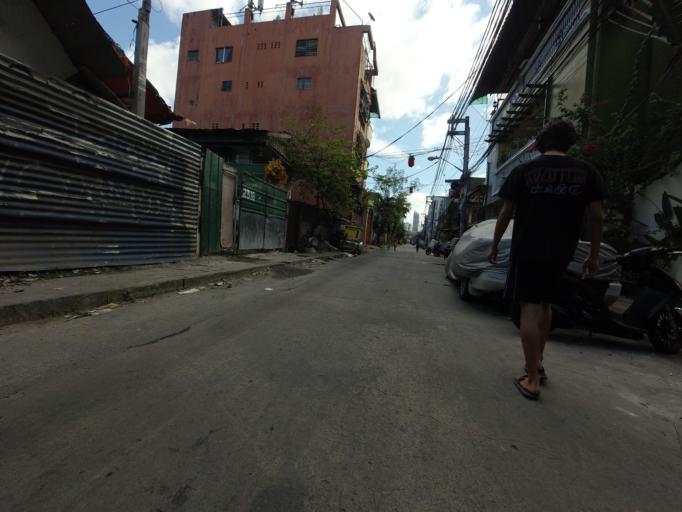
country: PH
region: Metro Manila
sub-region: City of Manila
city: Quiapo
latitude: 14.5756
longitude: 121.0057
